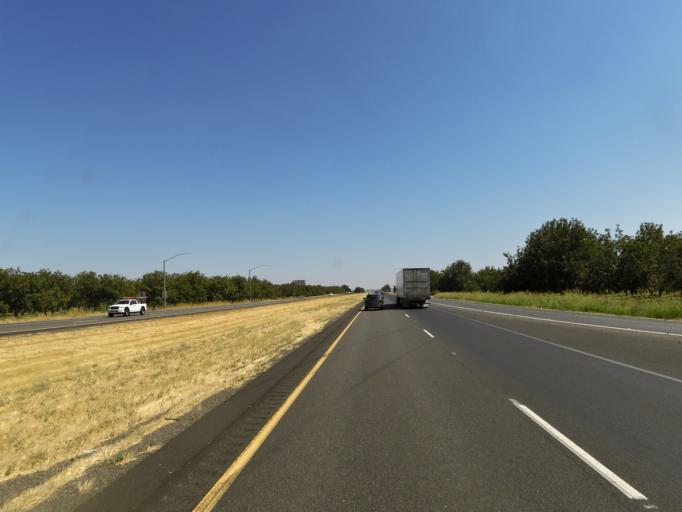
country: US
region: California
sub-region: Yolo County
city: Woodland
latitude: 38.7171
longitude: -121.7989
